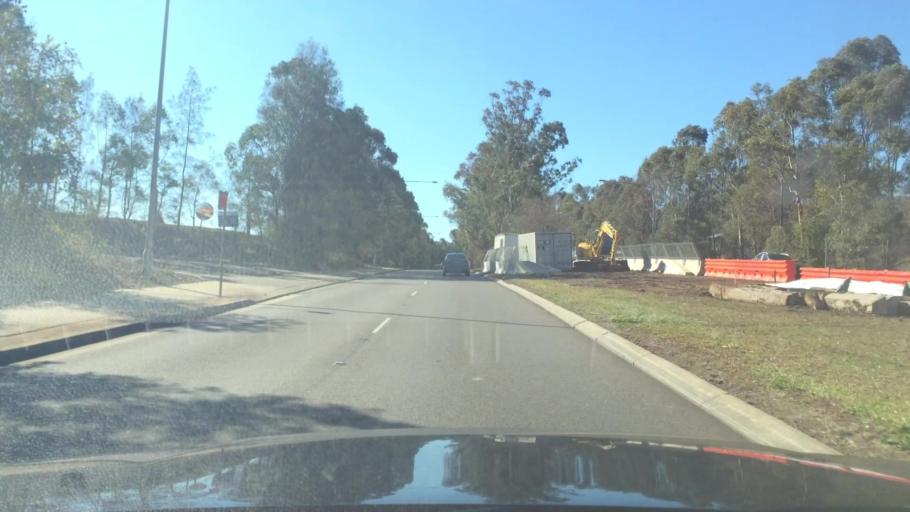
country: AU
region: New South Wales
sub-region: Fairfield
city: Cecil Park
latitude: -33.8886
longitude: 150.8611
